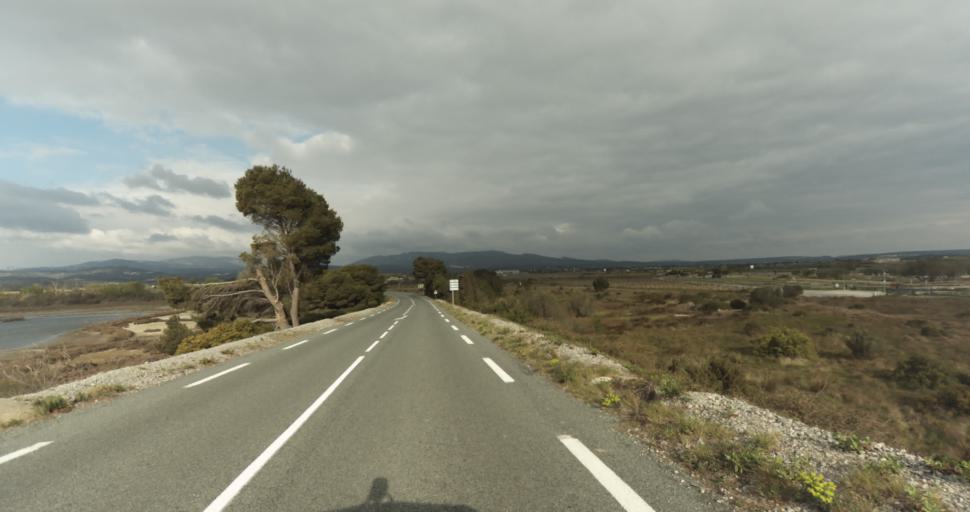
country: FR
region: Languedoc-Roussillon
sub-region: Departement de l'Aude
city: Leucate
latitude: 42.9290
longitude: 3.0087
